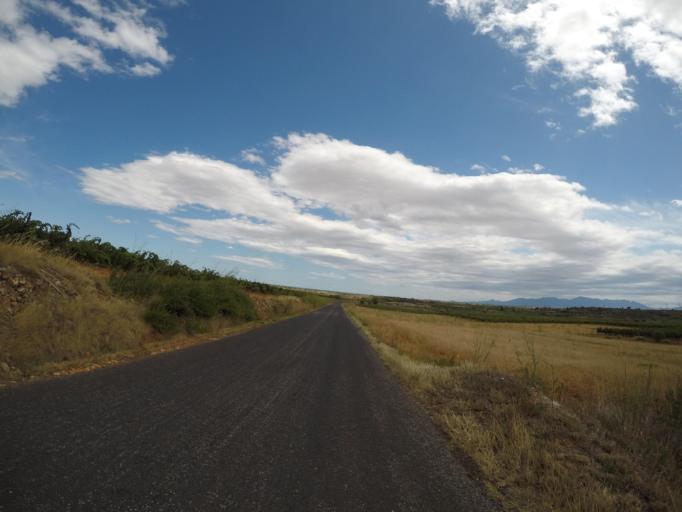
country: FR
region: Languedoc-Roussillon
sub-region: Departement des Pyrenees-Orientales
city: Baixas
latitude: 42.7500
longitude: 2.7897
